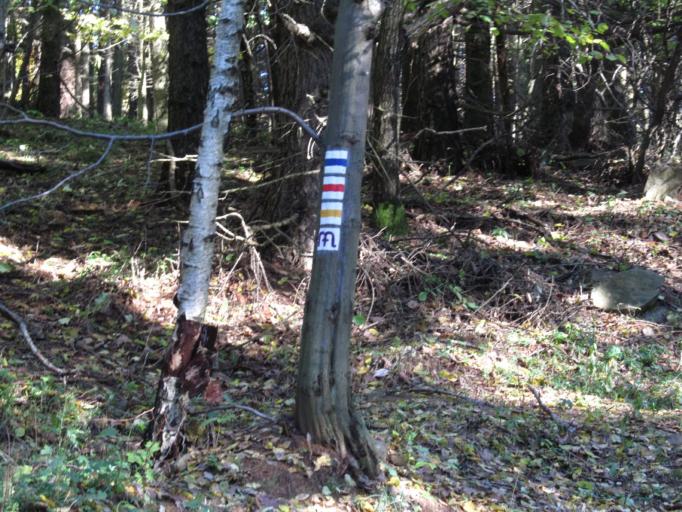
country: HU
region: Heves
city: Paradsasvar
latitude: 47.9179
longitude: 19.9104
